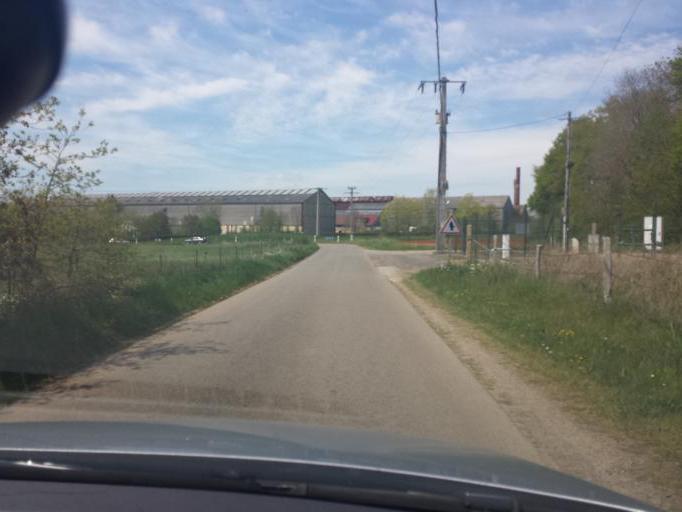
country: FR
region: Haute-Normandie
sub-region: Departement de l'Eure
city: Breteuil
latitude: 48.8195
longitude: 0.9255
